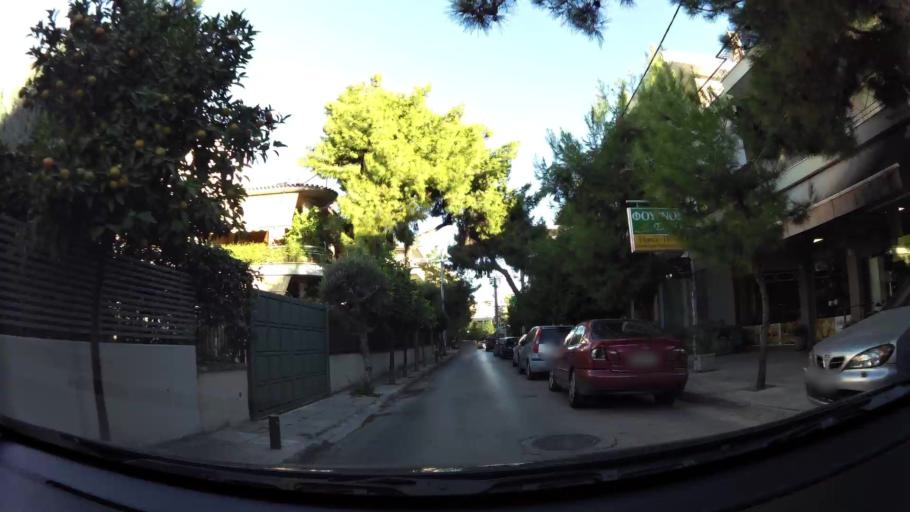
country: GR
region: Attica
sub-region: Nomarchia Athinas
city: Cholargos
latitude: 38.0079
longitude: 23.7962
